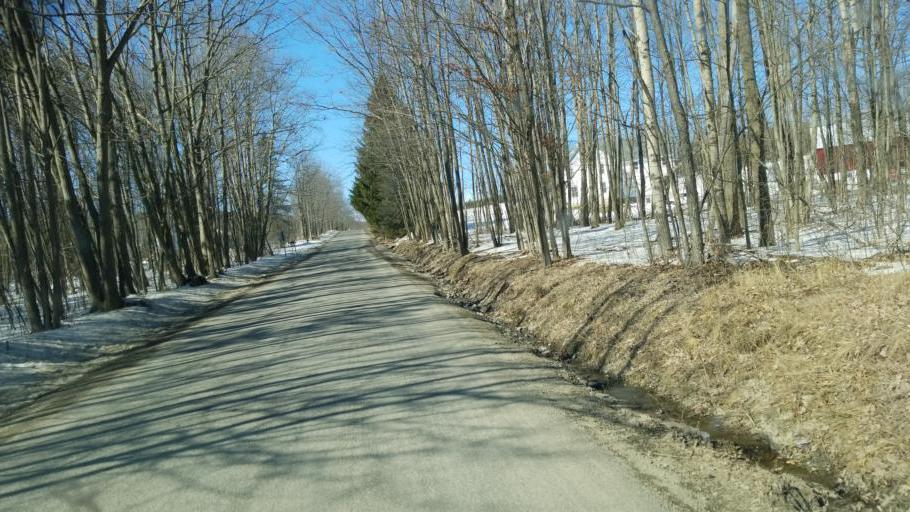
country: US
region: Pennsylvania
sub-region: Tioga County
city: Westfield
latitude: 41.9855
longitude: -77.6710
